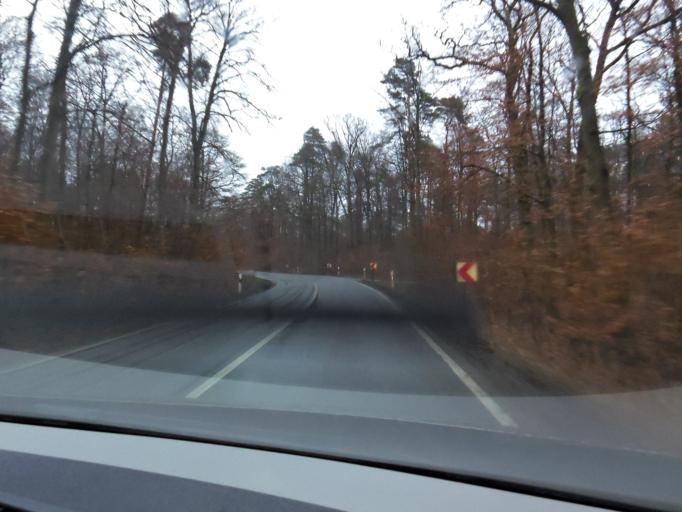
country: DE
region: Schleswig-Holstein
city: Fredeburg
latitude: 53.6490
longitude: 10.7356
